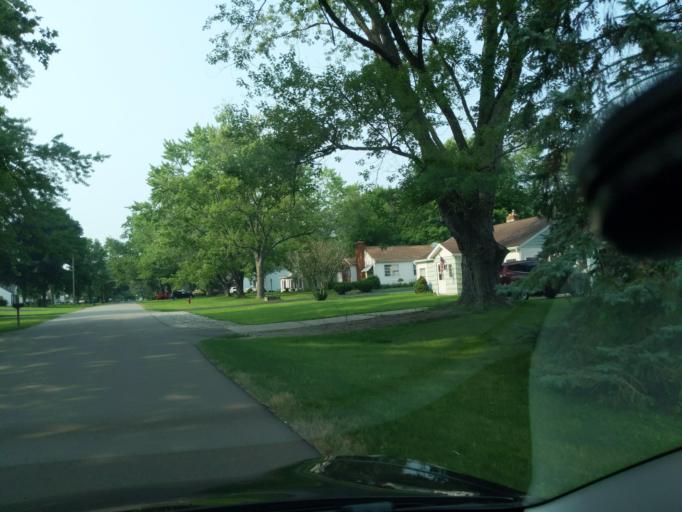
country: US
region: Michigan
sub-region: Jackson County
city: Jackson
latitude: 42.2354
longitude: -84.4471
